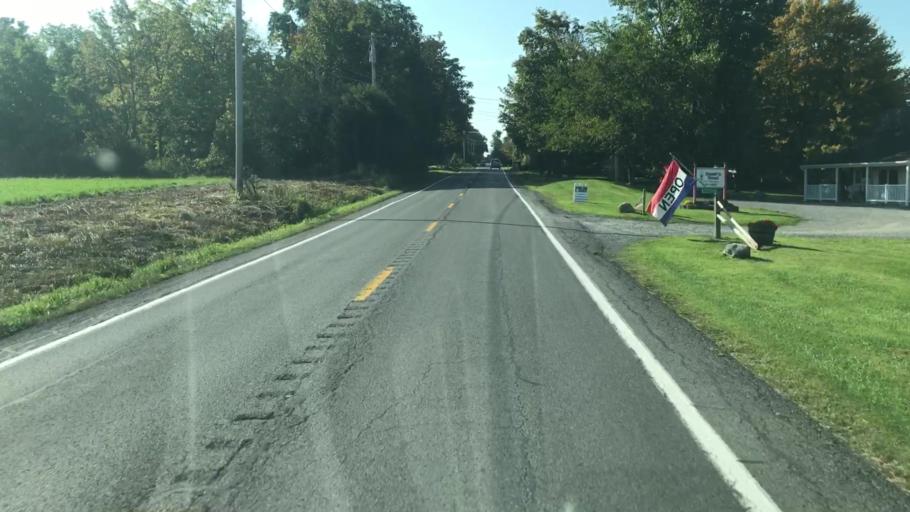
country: US
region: New York
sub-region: Onondaga County
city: Skaneateles
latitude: 42.9885
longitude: -76.4288
